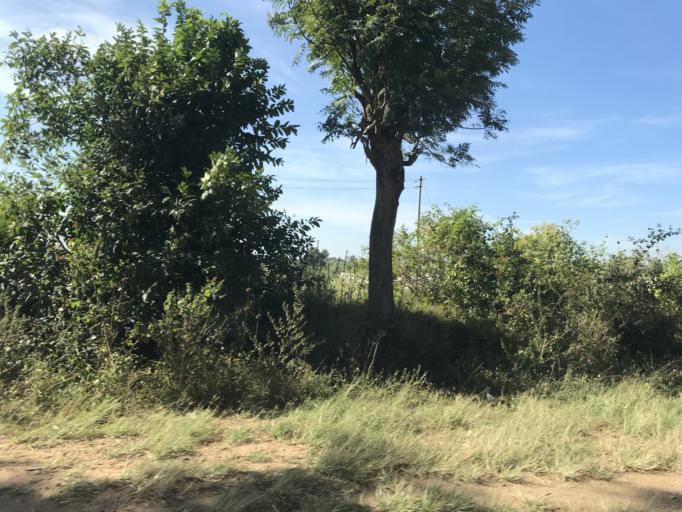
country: IN
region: Karnataka
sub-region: Mysore
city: Mysore
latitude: 12.2283
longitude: 76.5885
